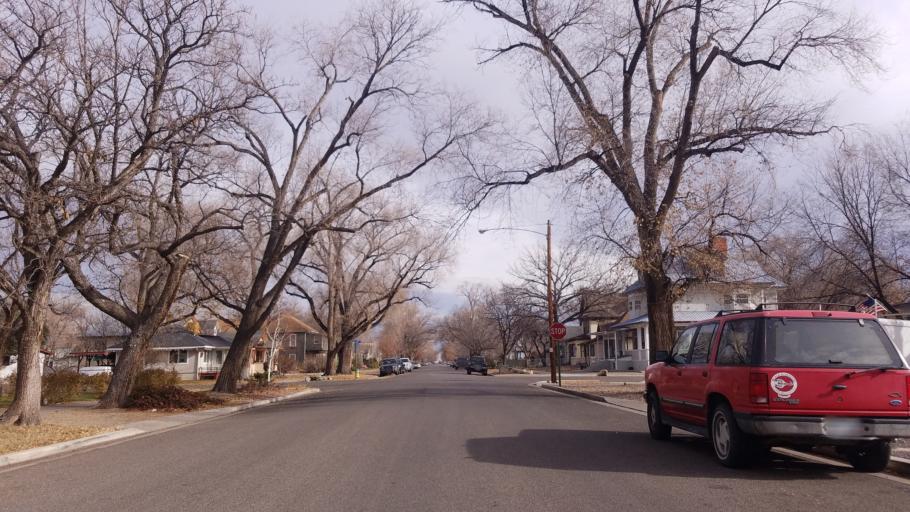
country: US
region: Colorado
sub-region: Mesa County
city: Grand Junction
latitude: 39.0683
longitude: -108.5566
